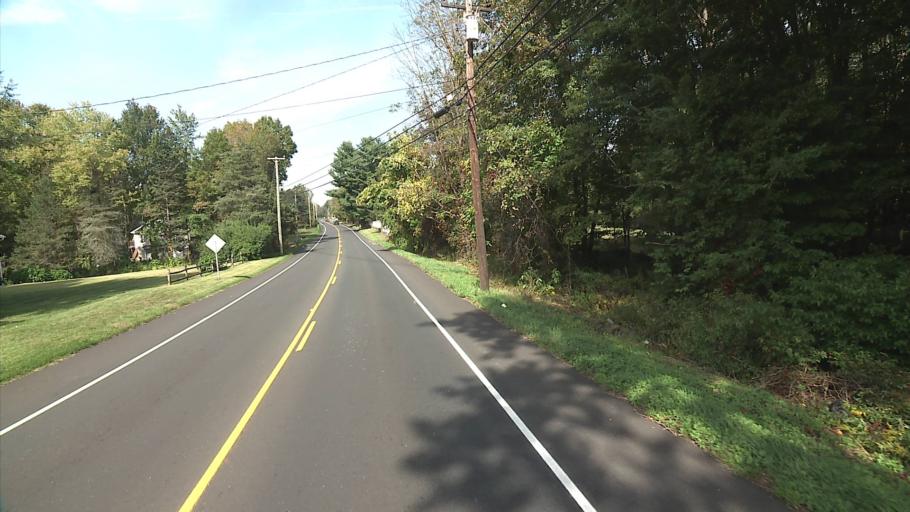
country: US
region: Connecticut
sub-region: Fairfield County
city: Newtown
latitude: 41.4034
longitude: -73.2502
